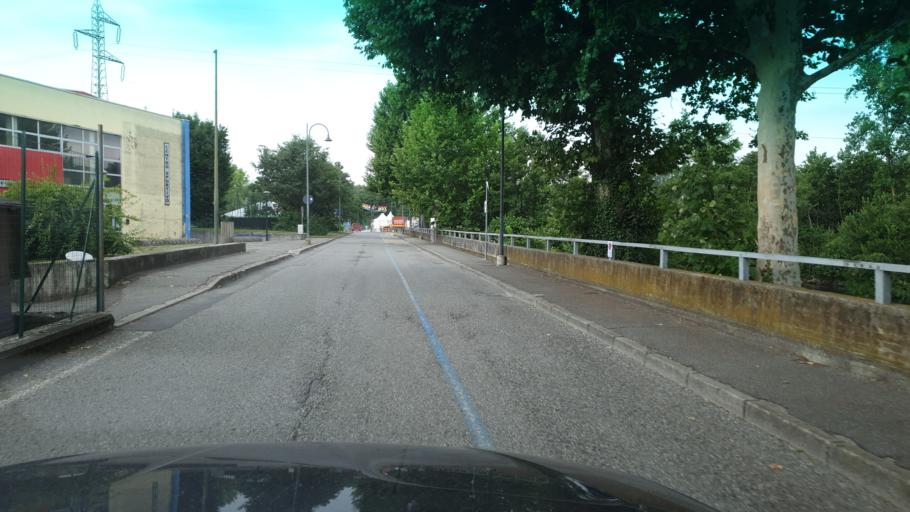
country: IT
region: Lombardy
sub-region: Provincia di Bergamo
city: Fara Gera d'Adda
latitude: 45.5513
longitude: 9.5290
